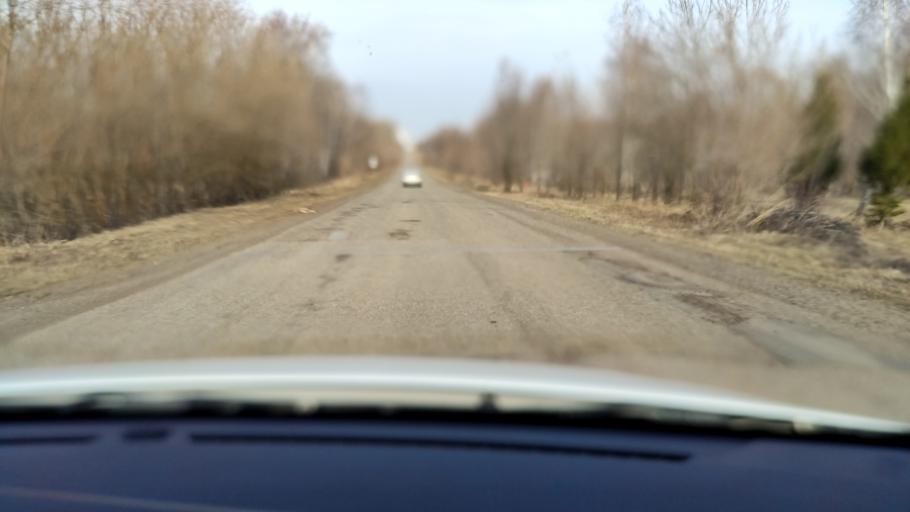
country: RU
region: Tatarstan
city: Stolbishchi
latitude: 55.7198
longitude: 49.2128
